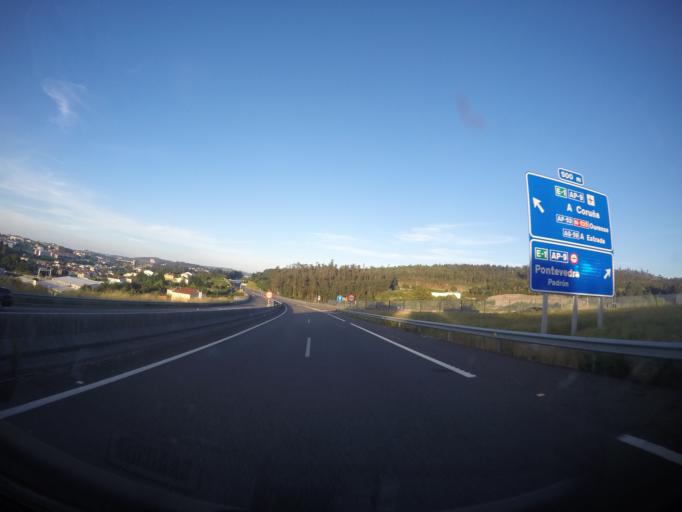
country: ES
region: Galicia
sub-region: Provincia da Coruna
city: Oroso
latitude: 42.9677
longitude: -8.4545
